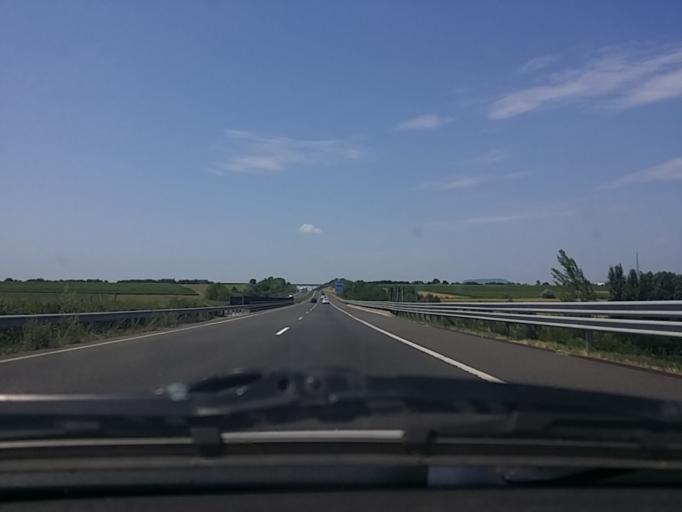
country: HU
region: Somogy
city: Balatonlelle
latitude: 46.7643
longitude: 17.6913
